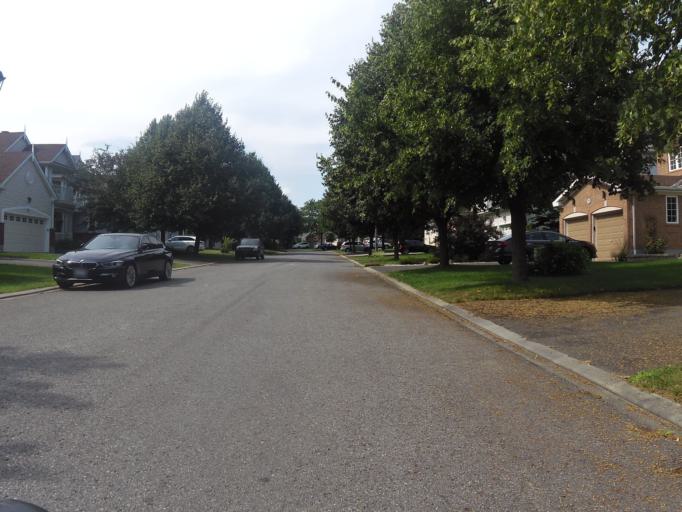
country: CA
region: Ontario
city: Bells Corners
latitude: 45.3116
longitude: -75.9220
